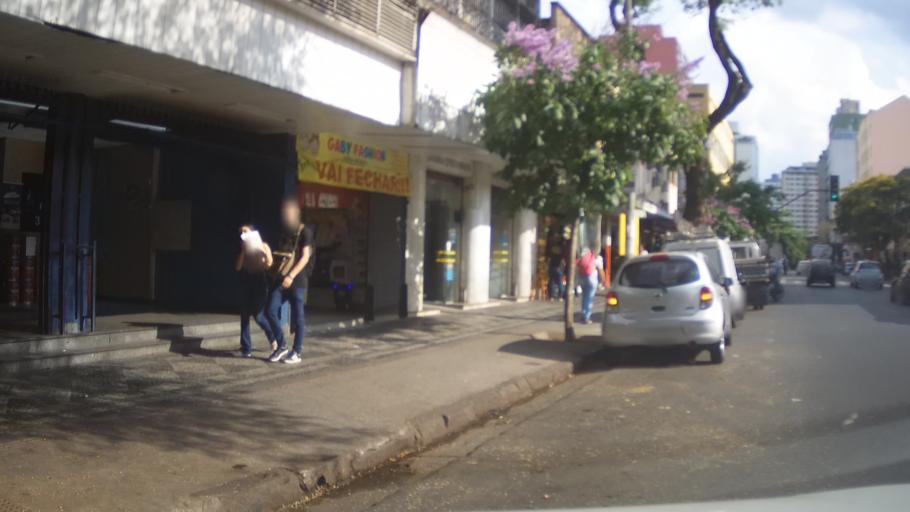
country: BR
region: Minas Gerais
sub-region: Belo Horizonte
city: Belo Horizonte
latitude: -19.9174
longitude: -43.9426
